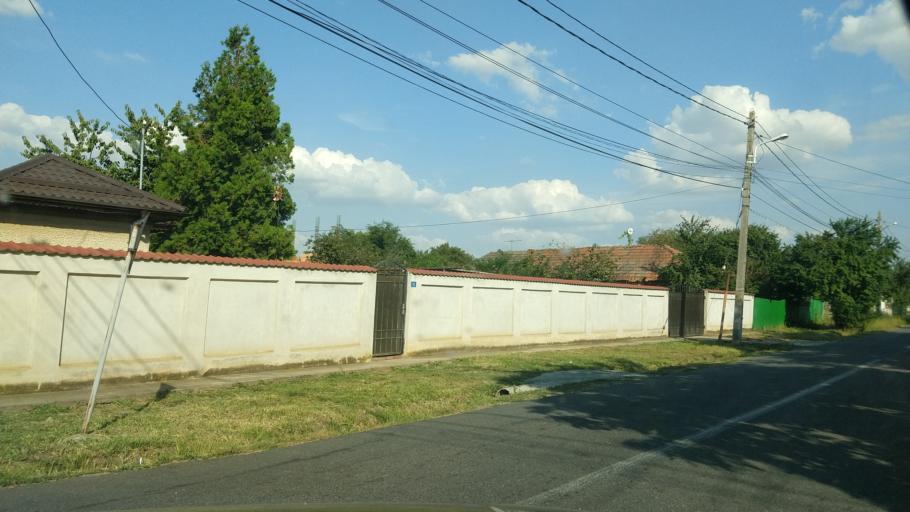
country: RO
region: Ilfov
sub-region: Comuna Afumati
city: Afumati
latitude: 44.5307
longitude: 26.2423
